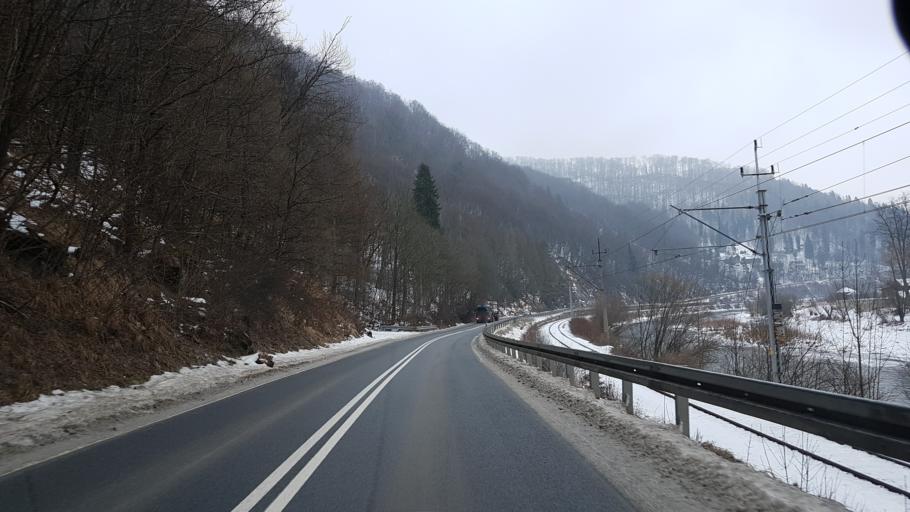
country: PL
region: Lesser Poland Voivodeship
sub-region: Powiat nowosadecki
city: Piwniczna-Zdroj
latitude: 49.4167
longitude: 20.7404
